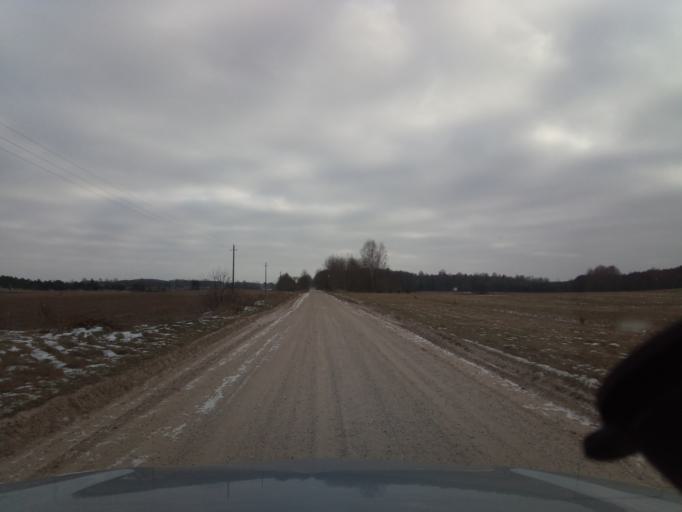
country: LT
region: Alytaus apskritis
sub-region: Alytaus rajonas
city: Daugai
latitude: 54.3220
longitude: 24.3248
